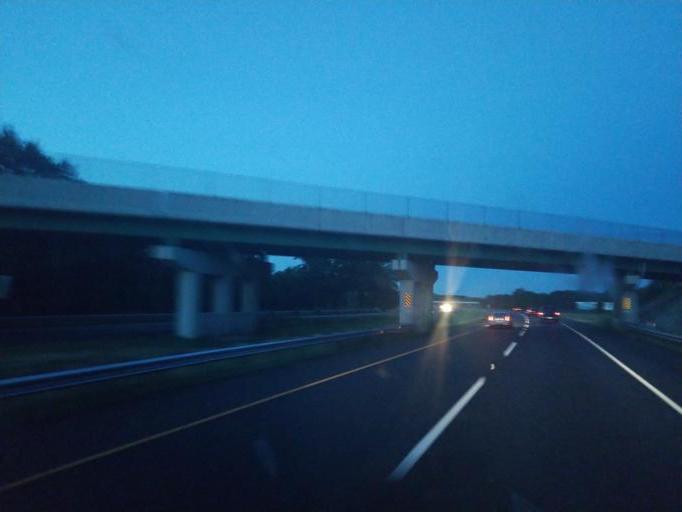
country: US
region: Indiana
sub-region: Saint Joseph County
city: Granger
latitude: 41.7312
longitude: -86.0509
